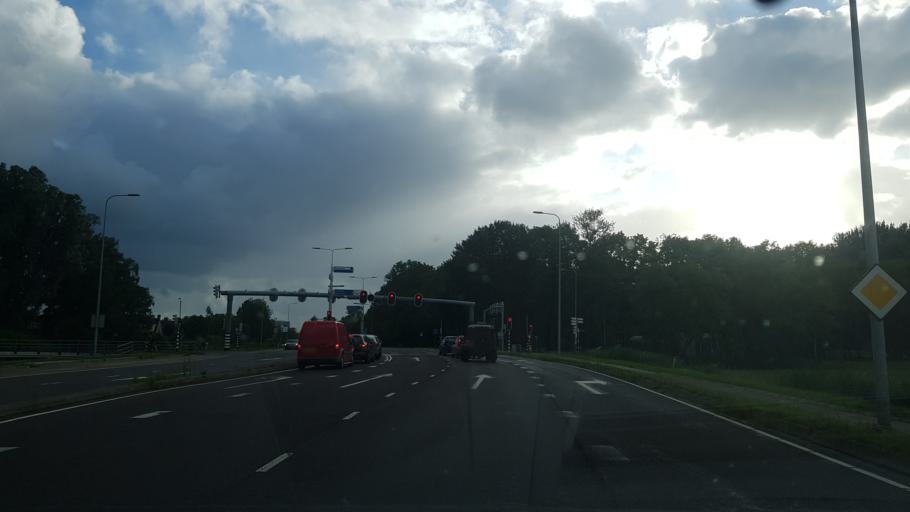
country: NL
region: Groningen
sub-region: Gemeente Groningen
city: Oosterpark
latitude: 53.2341
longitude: 6.6350
